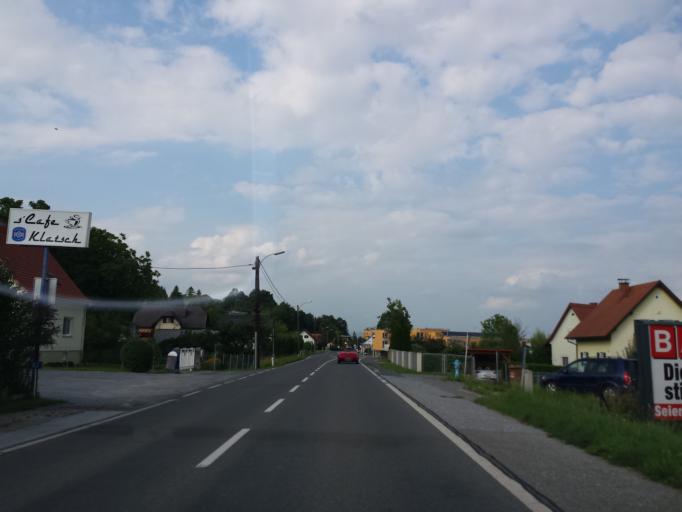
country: AT
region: Styria
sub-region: Politischer Bezirk Graz-Umgebung
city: Seiersberg
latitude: 47.0034
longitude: 15.3922
